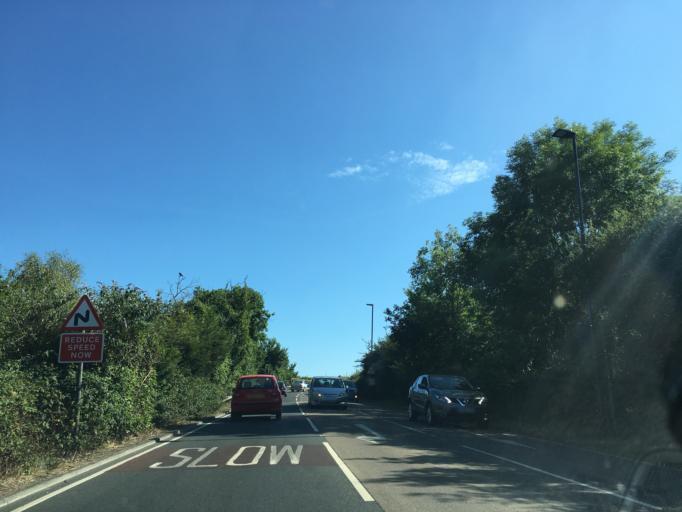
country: GB
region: England
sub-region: Isle of Wight
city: Brading
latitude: 50.6915
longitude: -1.1442
